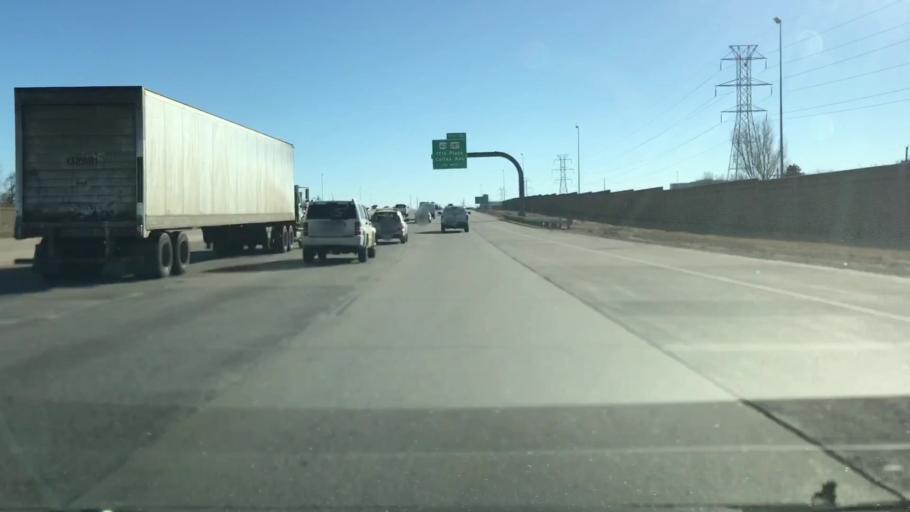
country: US
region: Colorado
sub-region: Adams County
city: Aurora
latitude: 39.7601
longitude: -104.8279
